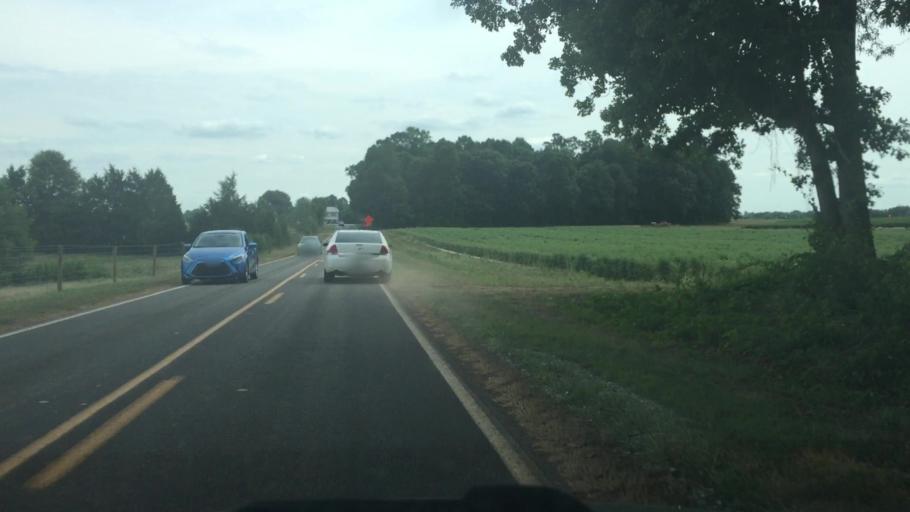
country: US
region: North Carolina
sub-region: Rowan County
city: Enochville
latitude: 35.6390
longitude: -80.6687
